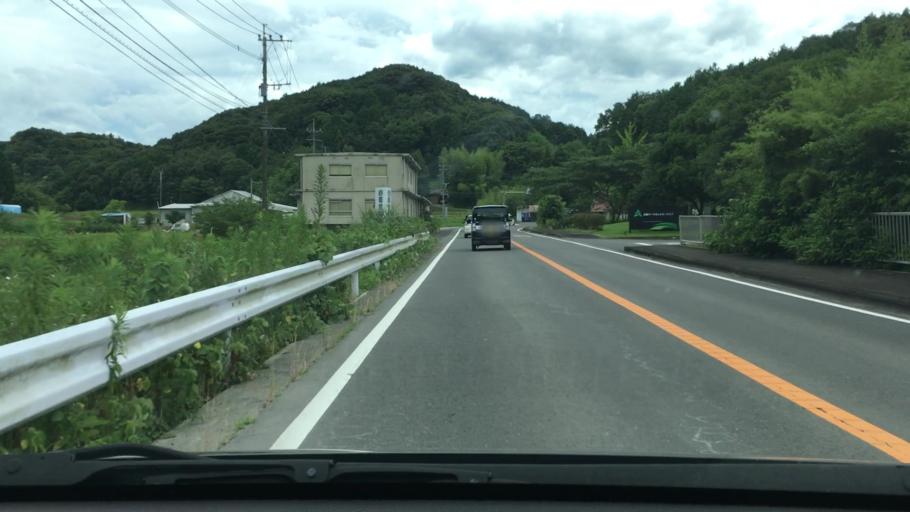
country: JP
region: Nagasaki
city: Togitsu
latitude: 32.9770
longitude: 129.7814
